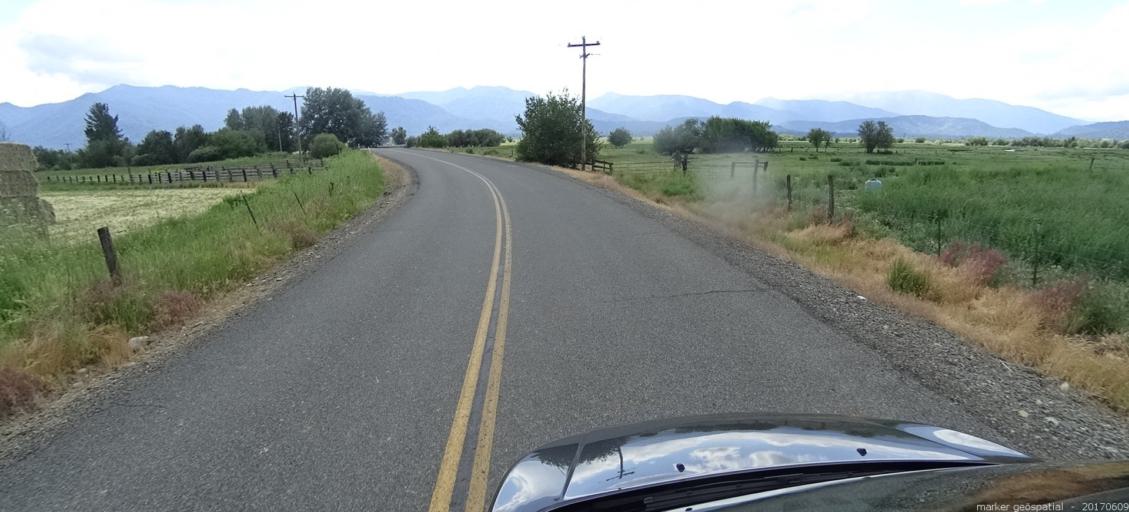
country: US
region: California
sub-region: Siskiyou County
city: Yreka
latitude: 41.5194
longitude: -122.8606
